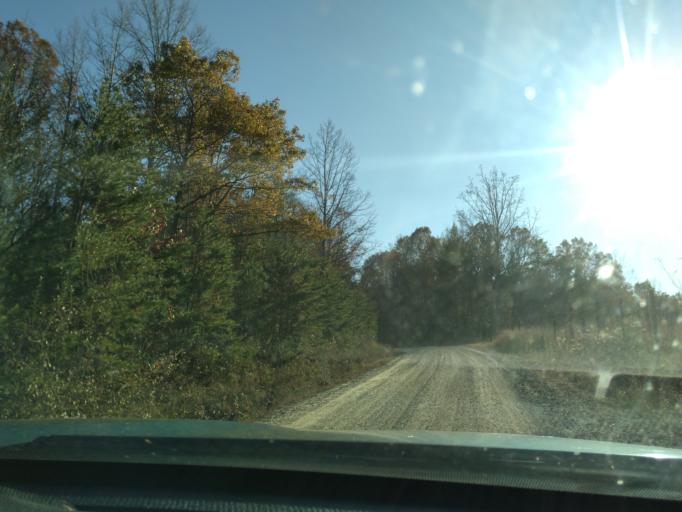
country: US
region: Virginia
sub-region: Floyd County
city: Floyd
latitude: 36.8343
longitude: -80.1968
